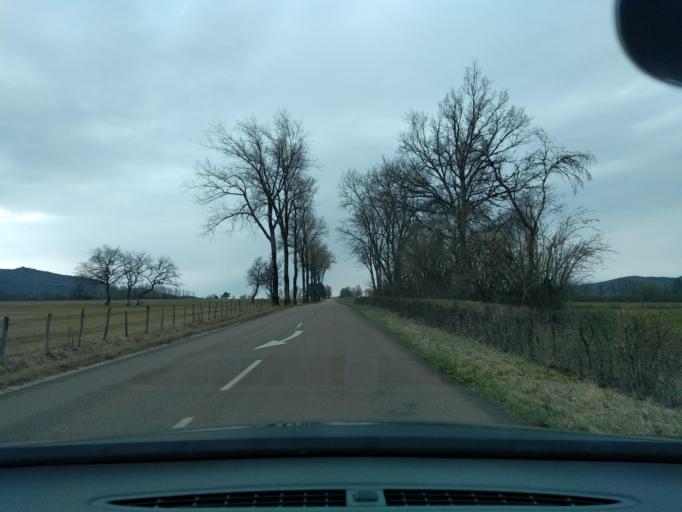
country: FR
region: Franche-Comte
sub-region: Departement du Jura
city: Arinthod
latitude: 46.3712
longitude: 5.5615
